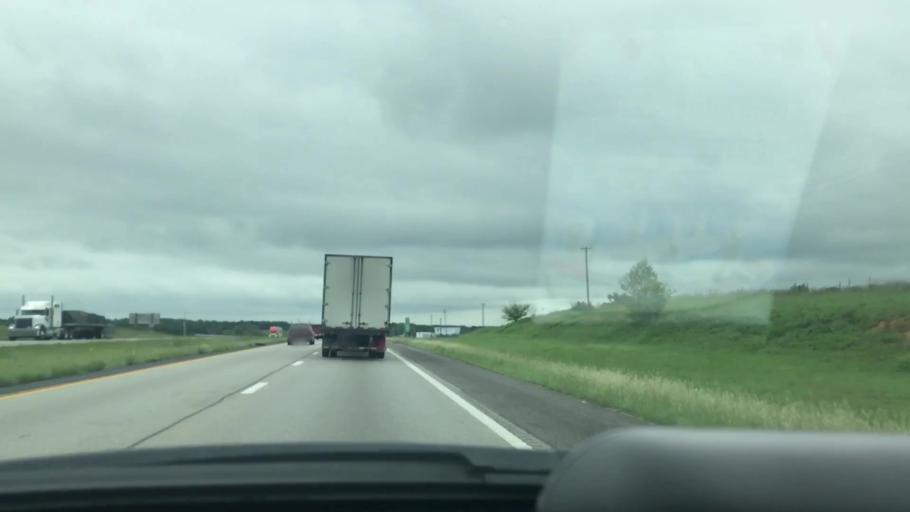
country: US
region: Missouri
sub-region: Christian County
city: Billings
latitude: 37.1852
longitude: -93.5914
